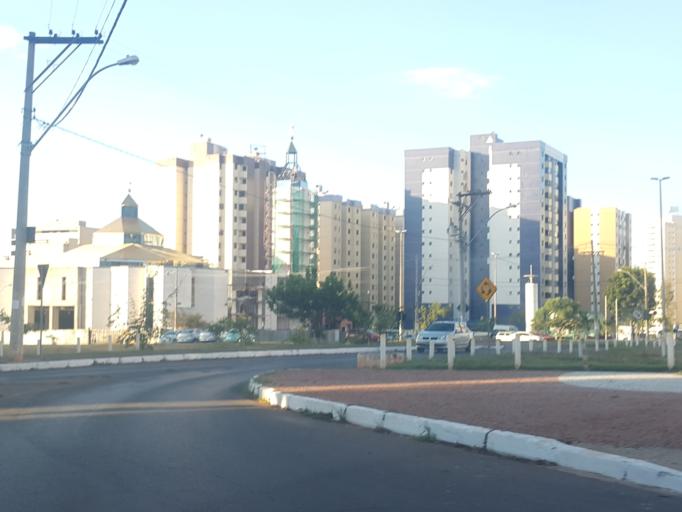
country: BR
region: Federal District
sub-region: Brasilia
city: Brasilia
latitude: -15.8342
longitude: -48.0184
